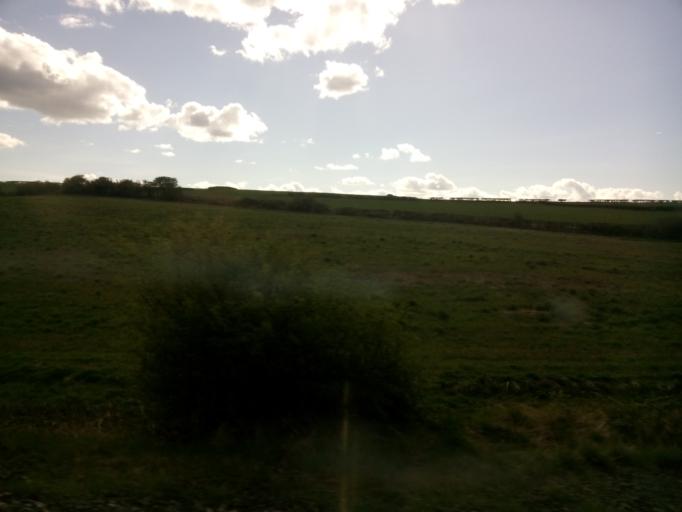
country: GB
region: England
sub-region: County Durham
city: Durham
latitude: 54.8161
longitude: -1.5749
